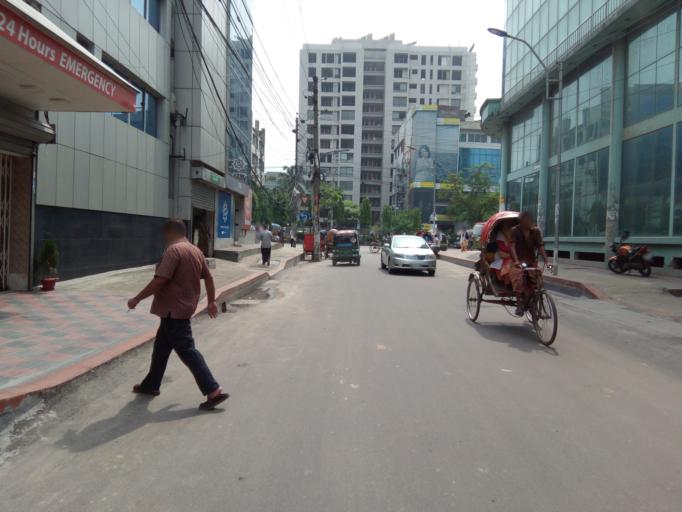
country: BD
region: Dhaka
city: Azimpur
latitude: 23.7454
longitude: 90.3822
